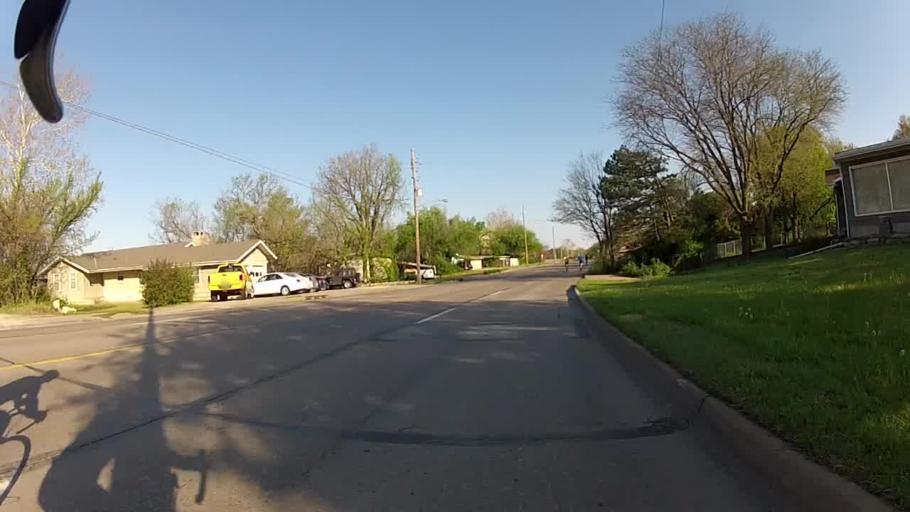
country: US
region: Kansas
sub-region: Riley County
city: Manhattan
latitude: 39.1866
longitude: -96.5970
